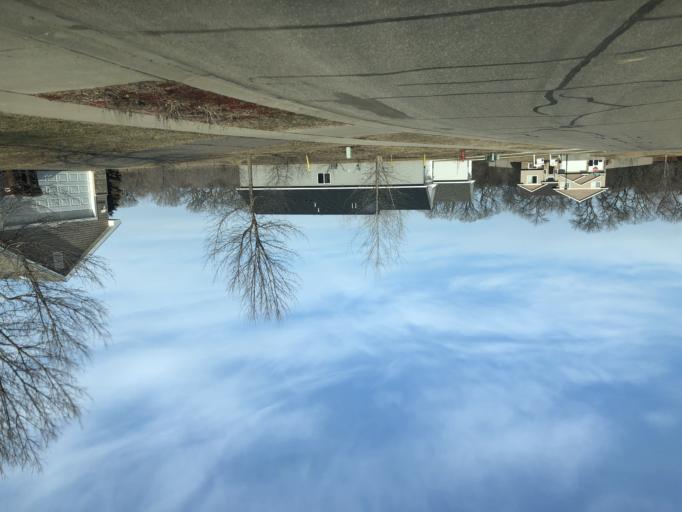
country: US
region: Minnesota
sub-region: Sherburne County
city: Becker
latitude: 45.4015
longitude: -93.8525
